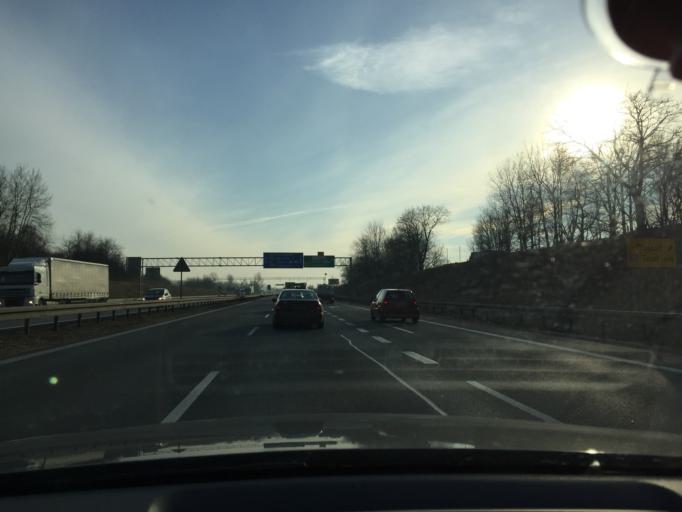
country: PL
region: Lesser Poland Voivodeship
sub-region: Powiat krakowski
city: Balice
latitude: 50.0787
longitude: 19.8085
